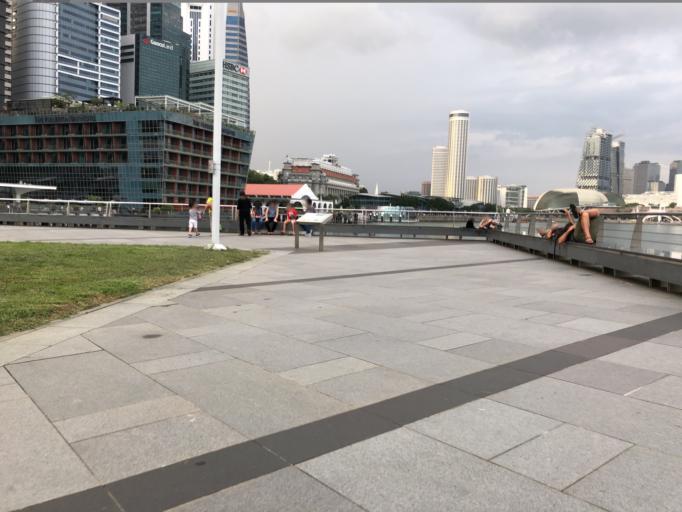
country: SG
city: Singapore
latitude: 1.2820
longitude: 103.8546
